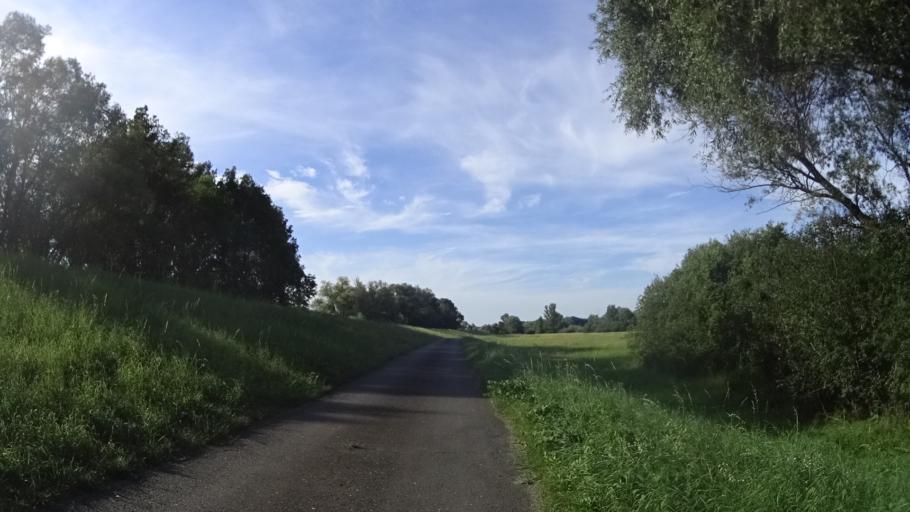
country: AT
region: Lower Austria
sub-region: Politischer Bezirk Ganserndorf
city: Drosing
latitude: 48.5571
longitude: 16.9590
